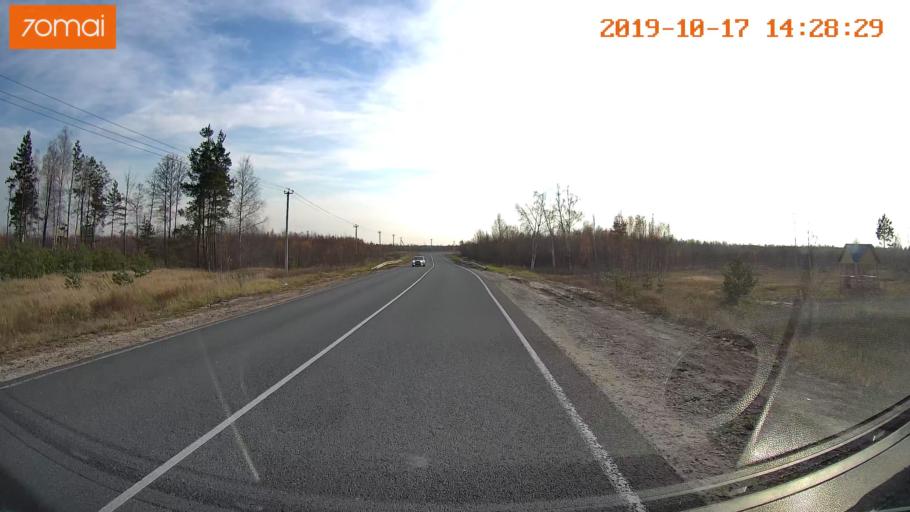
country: RU
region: Rjazan
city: Solotcha
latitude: 54.9726
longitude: 39.9511
